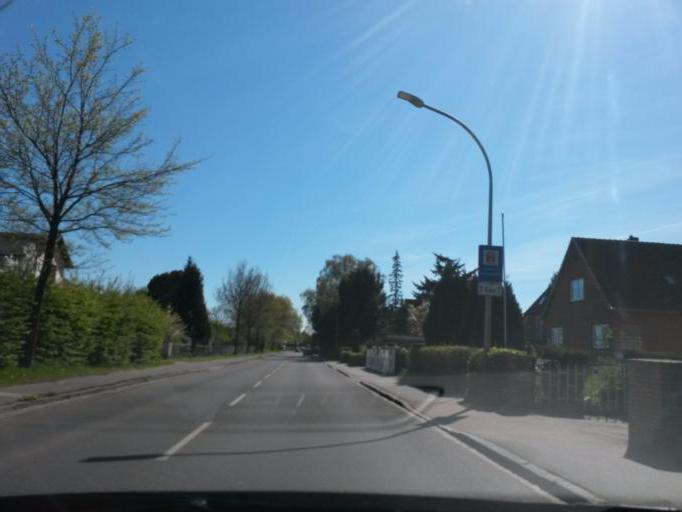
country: DE
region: Schleswig-Holstein
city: Rellingen
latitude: 53.6232
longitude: 9.8238
